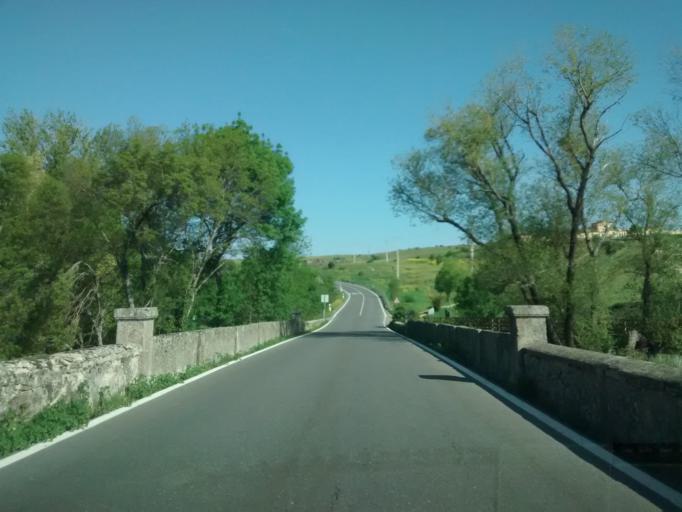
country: ES
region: Castille and Leon
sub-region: Provincia de Segovia
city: San Ildefonso
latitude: 40.9122
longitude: -4.0132
